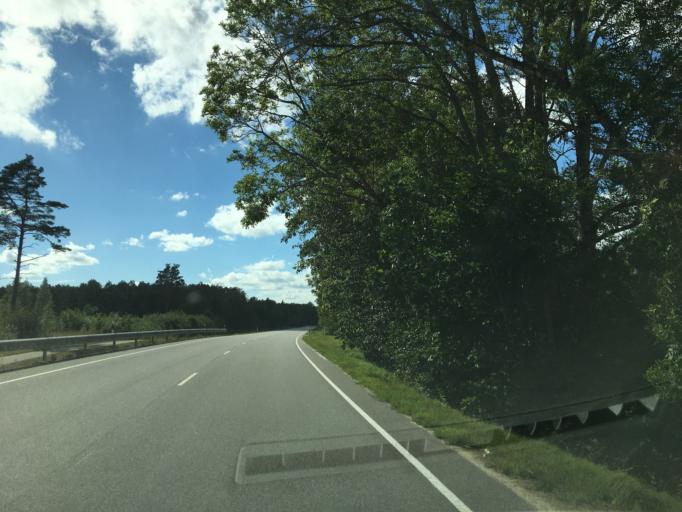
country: EE
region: Paernumaa
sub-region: Vaendra vald (alev)
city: Vandra
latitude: 58.6426
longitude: 25.0897
